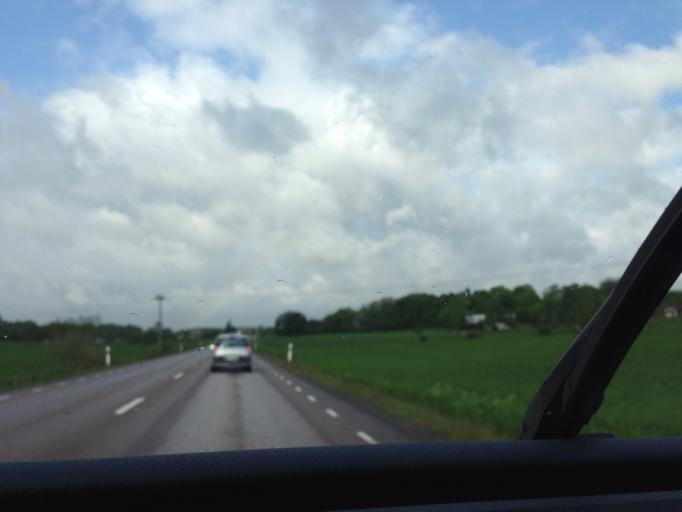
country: SE
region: Vaestra Goetaland
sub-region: Skovde Kommun
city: Stopen
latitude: 58.4041
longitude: 13.9908
